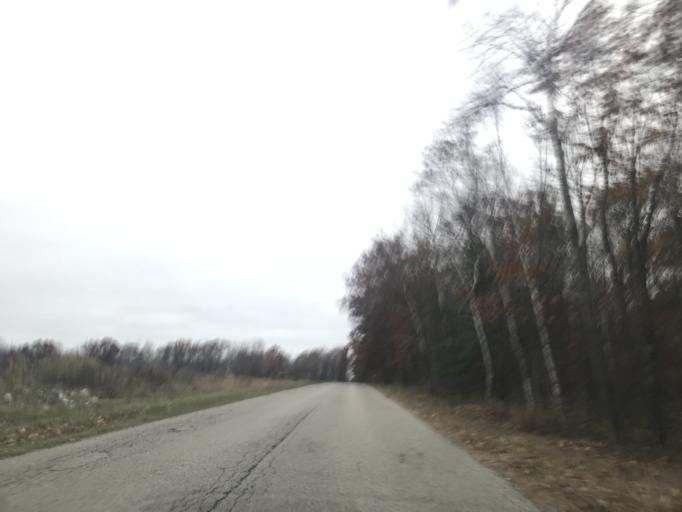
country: US
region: Wisconsin
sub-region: Marinette County
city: Peshtigo
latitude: 45.1233
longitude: -87.7498
